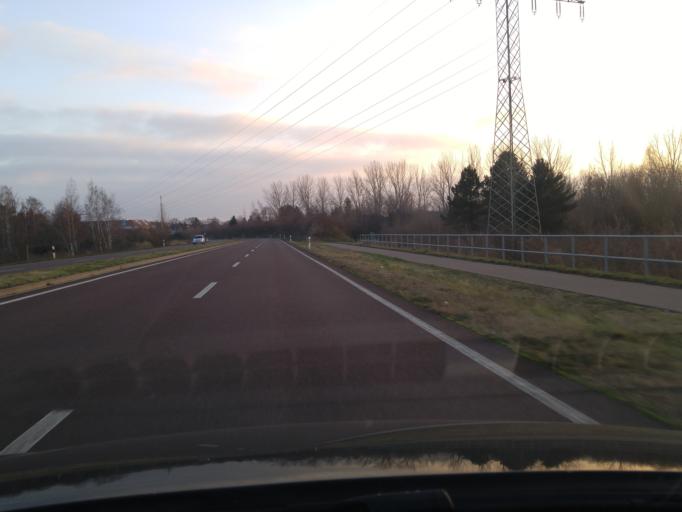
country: DE
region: Saxony
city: Leipzig
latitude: 51.3797
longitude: 12.3429
